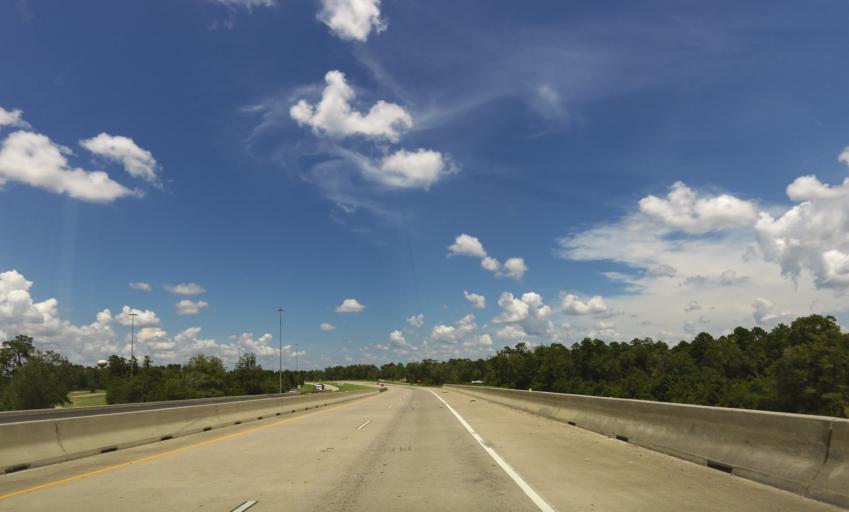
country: US
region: Texas
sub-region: San Jacinto County
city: Shepherd
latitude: 30.4726
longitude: -95.0119
